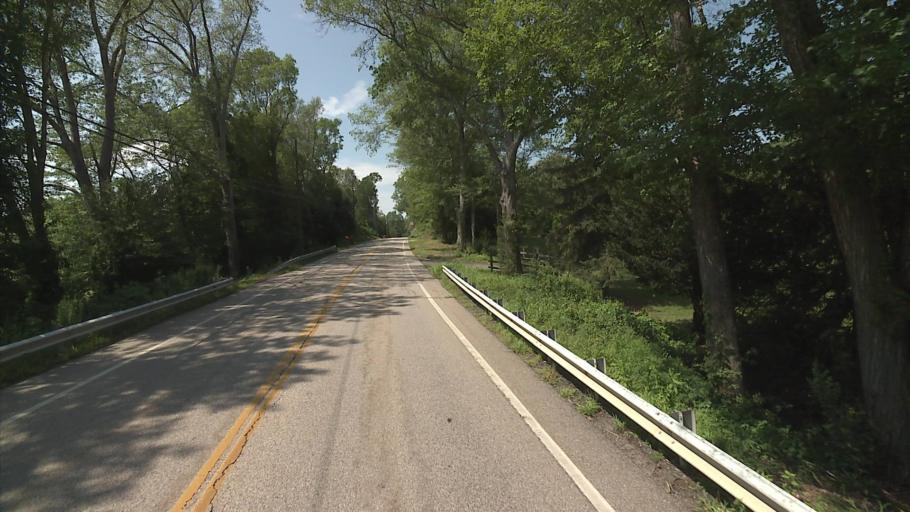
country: US
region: Connecticut
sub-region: New London County
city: Niantic
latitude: 41.4142
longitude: -72.2190
